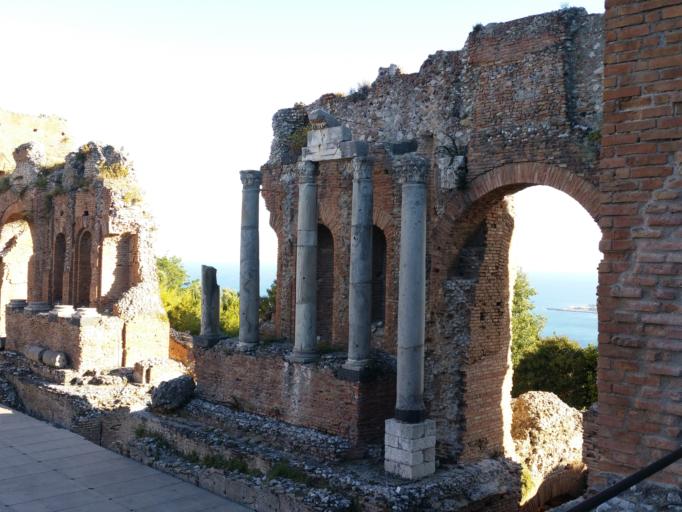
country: IT
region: Sicily
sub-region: Messina
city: Taormina
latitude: 37.8524
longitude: 15.2920
